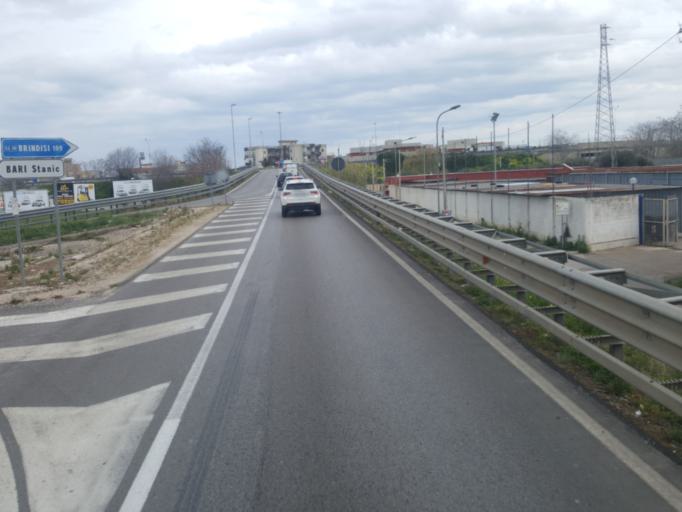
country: IT
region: Apulia
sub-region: Provincia di Bari
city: Modugno
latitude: 41.1048
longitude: 16.8178
